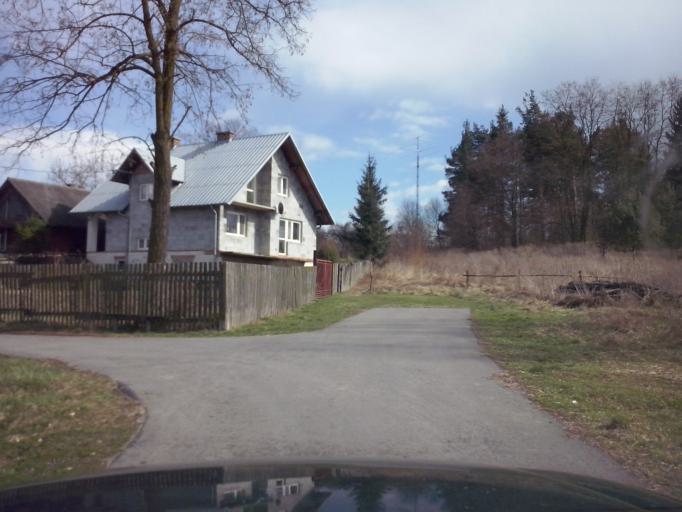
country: PL
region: Subcarpathian Voivodeship
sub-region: Powiat nizanski
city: Bieliny
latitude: 50.4400
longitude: 22.3076
